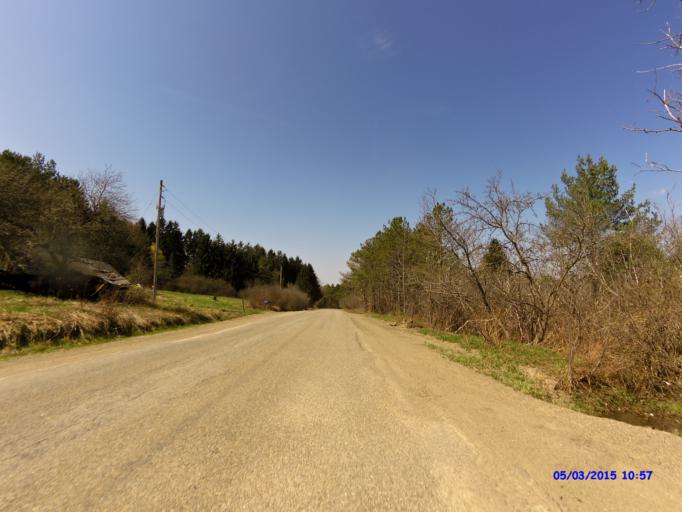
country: US
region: New York
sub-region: Cattaraugus County
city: Franklinville
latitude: 42.3386
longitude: -78.4413
